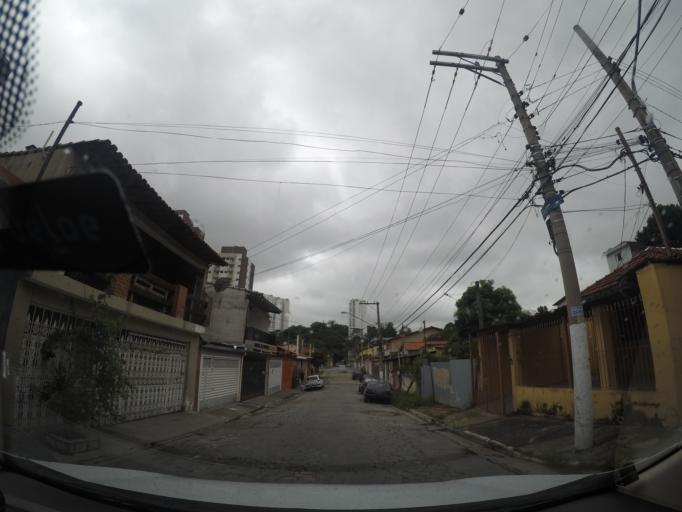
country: BR
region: Sao Paulo
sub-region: Osasco
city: Osasco
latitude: -23.5017
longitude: -46.7574
